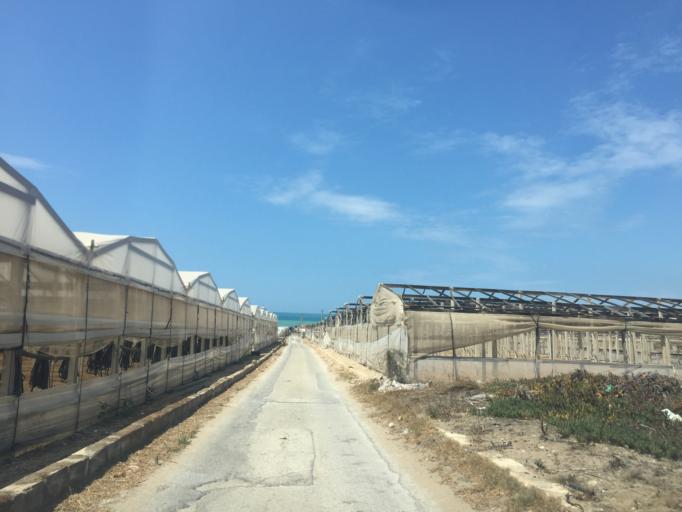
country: IT
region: Sicily
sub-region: Ragusa
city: Scoglitti
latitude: 36.9346
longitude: 14.4061
